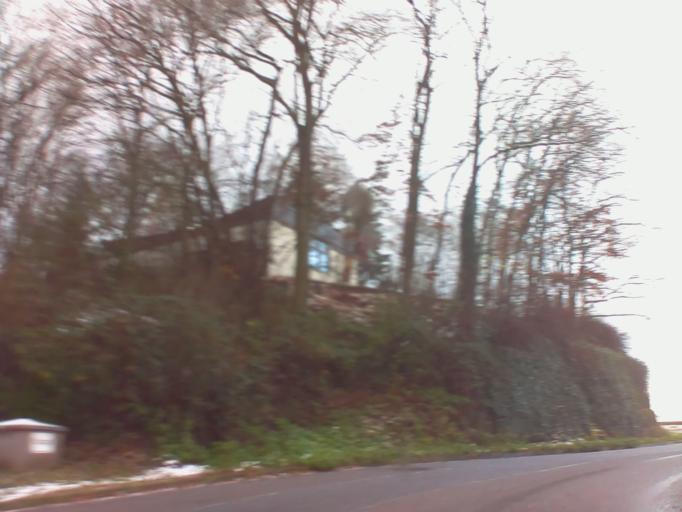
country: DE
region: Hesse
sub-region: Regierungsbezirk Darmstadt
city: Birkenau
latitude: 49.5461
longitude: 8.7471
